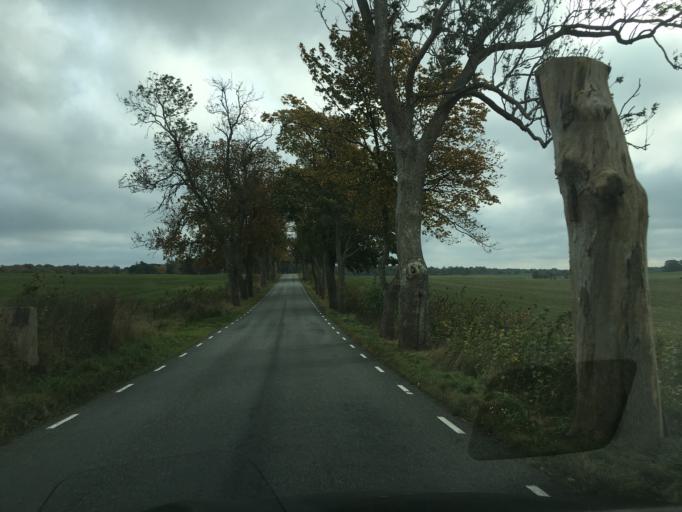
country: SE
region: Skane
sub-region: Tomelilla Kommun
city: Tomelilla
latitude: 55.6500
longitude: 14.0350
